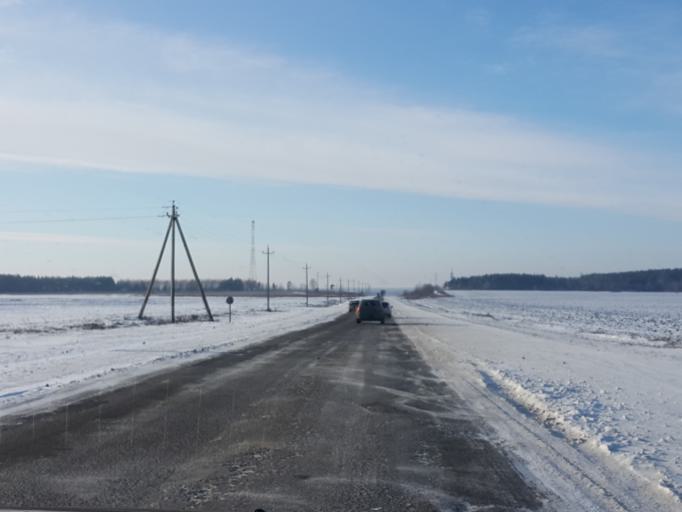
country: RU
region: Tambov
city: Znamenka
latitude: 52.4232
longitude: 41.5013
